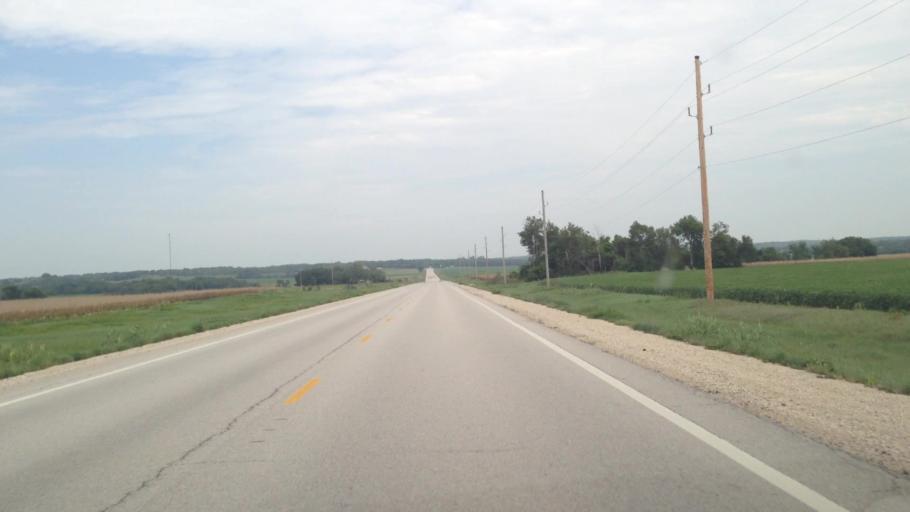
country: US
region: Kansas
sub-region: Anderson County
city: Garnett
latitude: 38.0611
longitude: -95.1693
